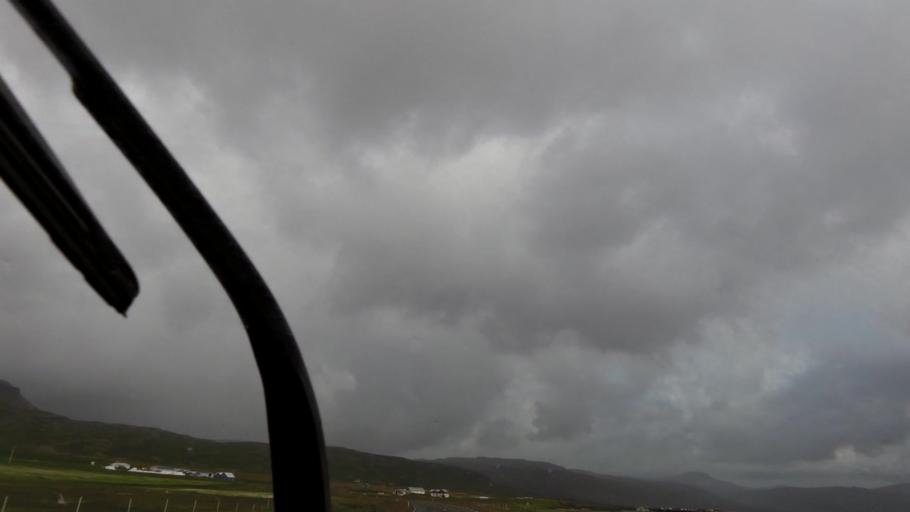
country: IS
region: Westfjords
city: Isafjoerdur
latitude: 65.5226
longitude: -23.1883
